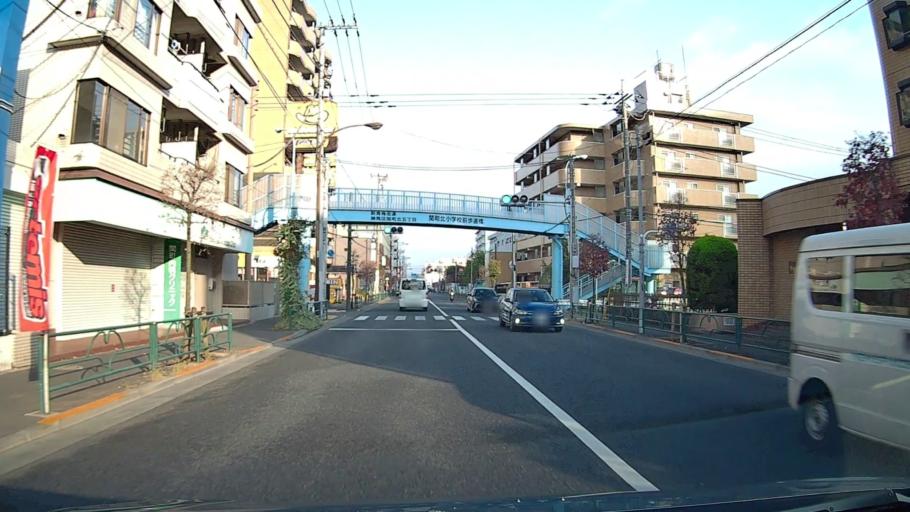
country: JP
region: Tokyo
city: Musashino
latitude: 35.7314
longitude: 139.5741
